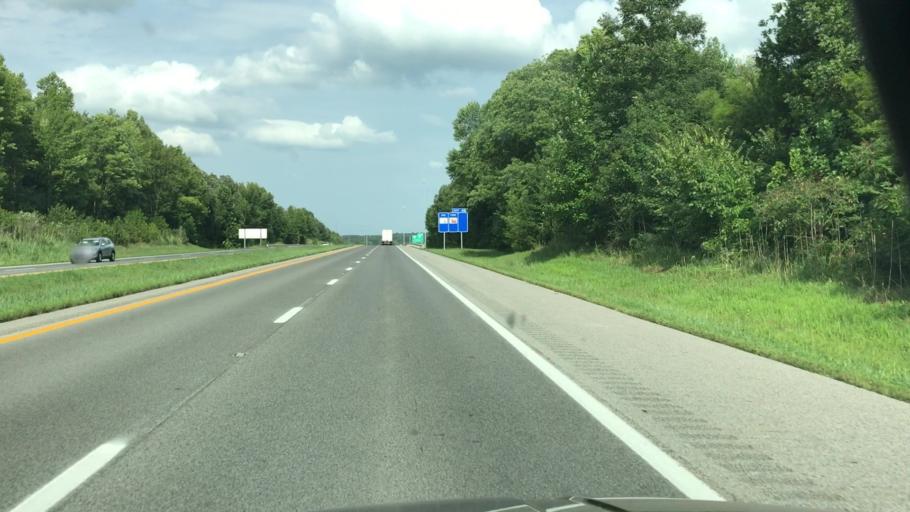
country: US
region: Kentucky
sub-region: Muhlenberg County
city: Greenville
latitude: 37.2321
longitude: -87.2851
